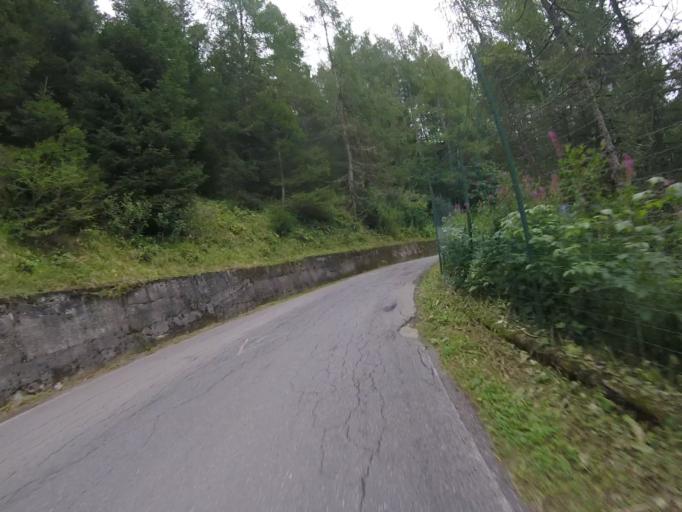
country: IT
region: Lombardy
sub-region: Provincia di Brescia
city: Monno
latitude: 46.2391
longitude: 10.3205
